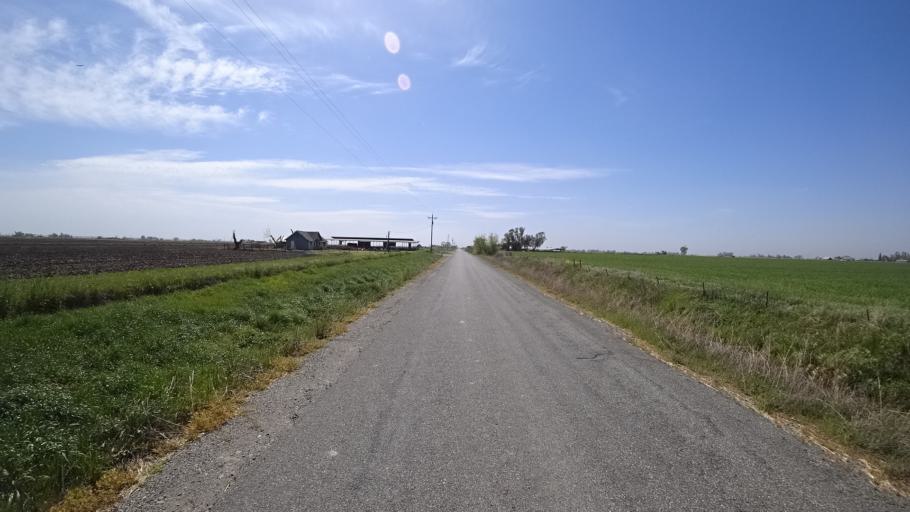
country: US
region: California
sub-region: Glenn County
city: Willows
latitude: 39.5789
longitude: -122.0839
